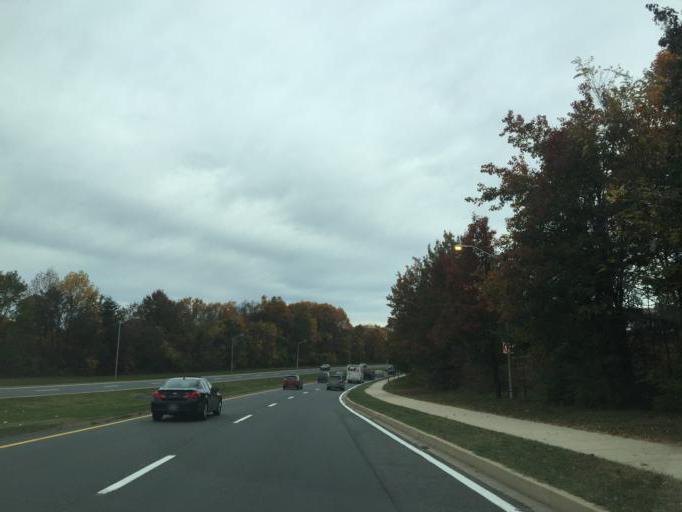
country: US
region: Maryland
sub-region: Montgomery County
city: Gaithersburg
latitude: 39.1118
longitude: -77.2202
